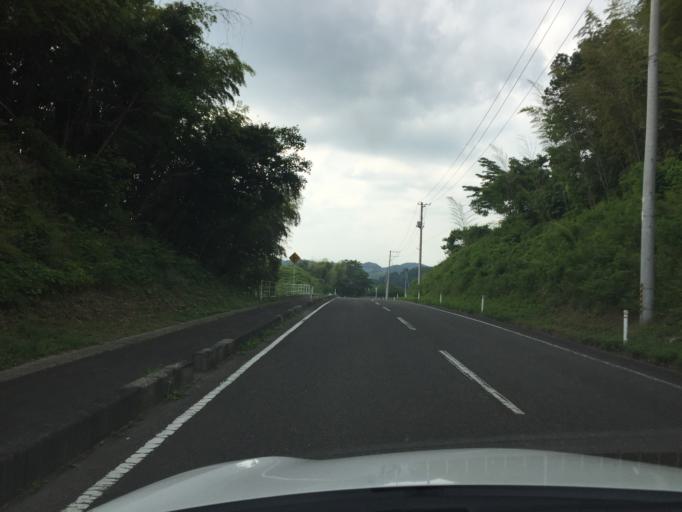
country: JP
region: Fukushima
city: Miharu
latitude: 37.4028
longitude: 140.4886
